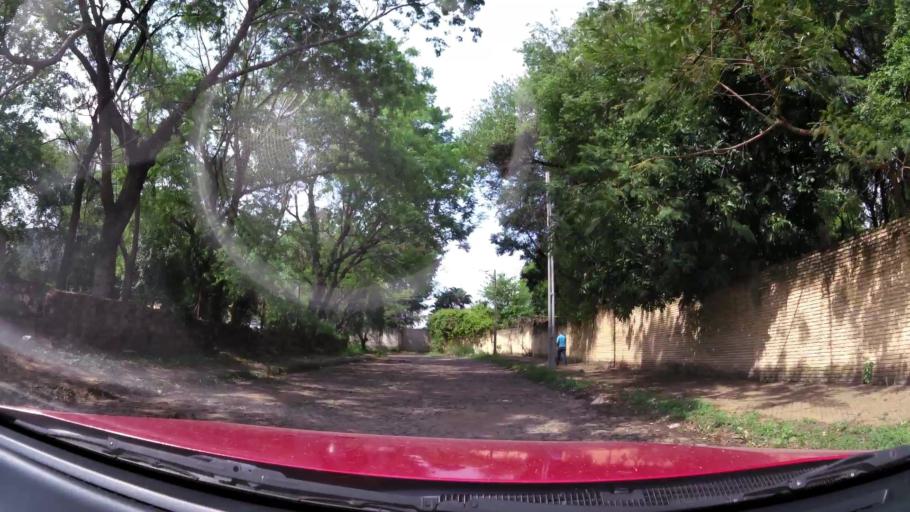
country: PY
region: Asuncion
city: Asuncion
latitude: -25.2681
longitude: -57.5641
